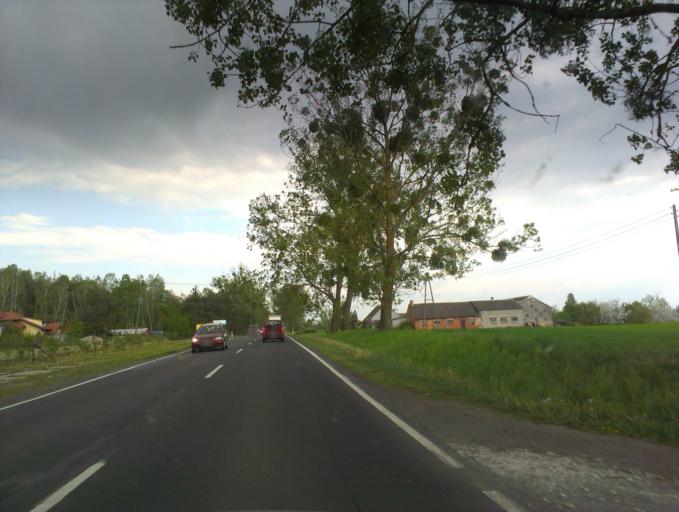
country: PL
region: Kujawsko-Pomorskie
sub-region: Powiat swiecki
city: Drzycim
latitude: 53.4234
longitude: 18.3341
